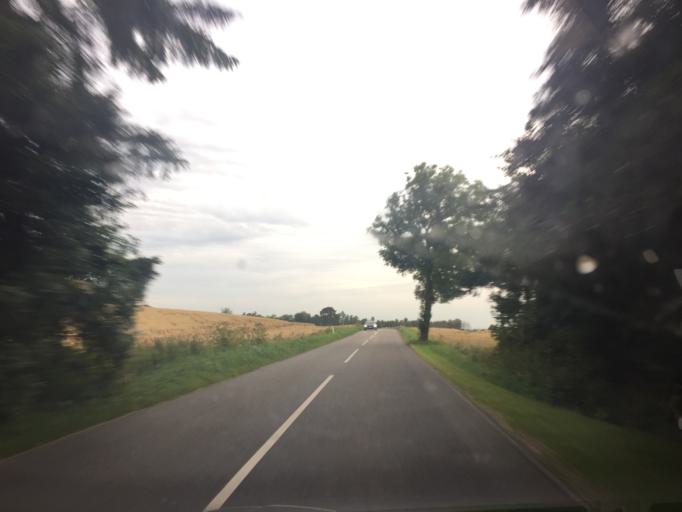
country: DK
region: Capital Region
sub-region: Egedal Kommune
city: Vekso
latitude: 55.7017
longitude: 12.2300
